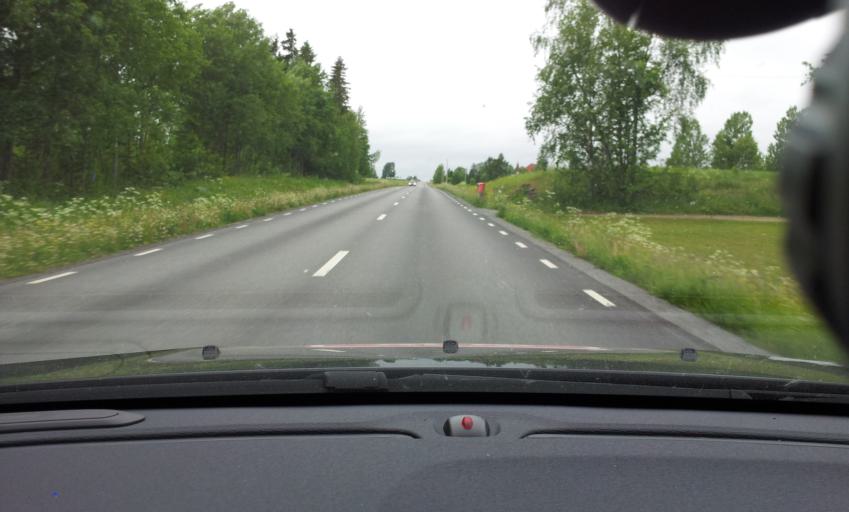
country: SE
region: Jaemtland
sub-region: Bergs Kommun
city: Hoverberg
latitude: 62.9945
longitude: 14.4092
